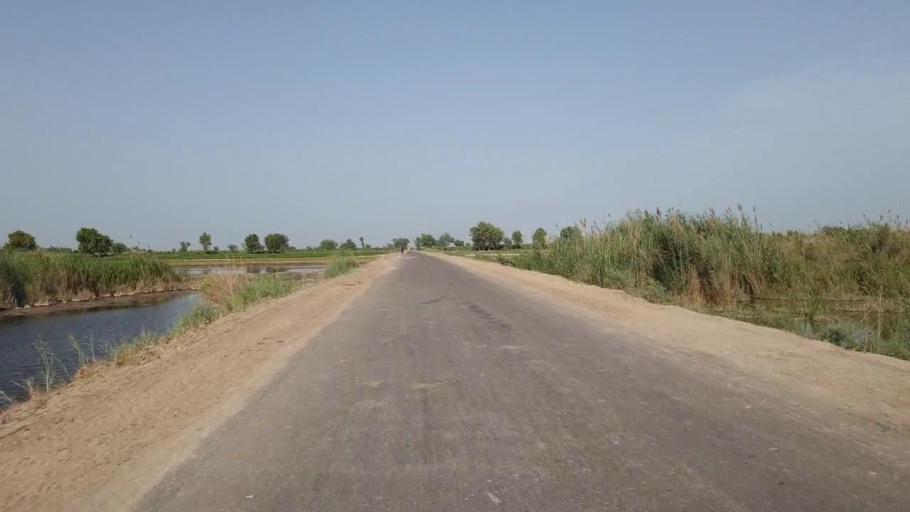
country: PK
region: Sindh
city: Sakrand
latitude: 26.2842
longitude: 68.2589
